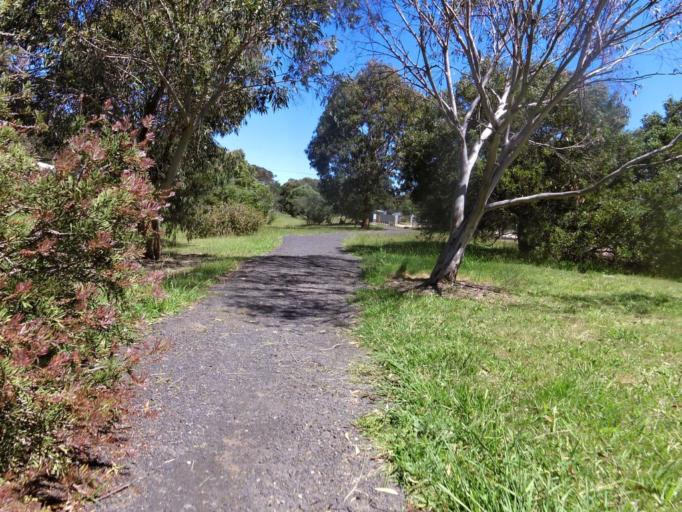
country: AU
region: Victoria
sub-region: Whittlesea
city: Whittlesea
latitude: -37.3621
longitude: 145.0351
